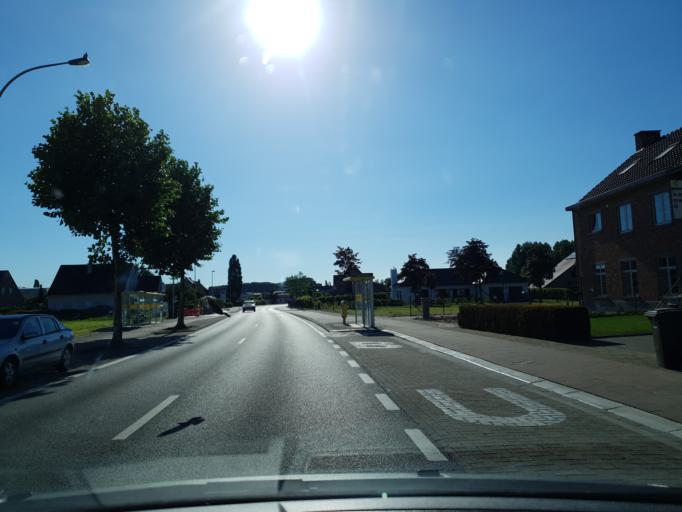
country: BE
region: Flanders
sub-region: Provincie Antwerpen
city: Wuustwezel
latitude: 51.4002
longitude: 4.6330
